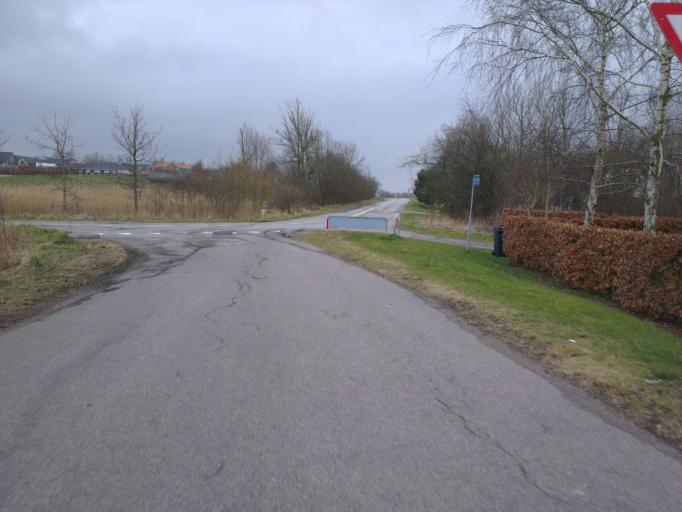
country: DK
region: Capital Region
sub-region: Frederikssund Kommune
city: Frederikssund
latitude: 55.8696
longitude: 12.0685
